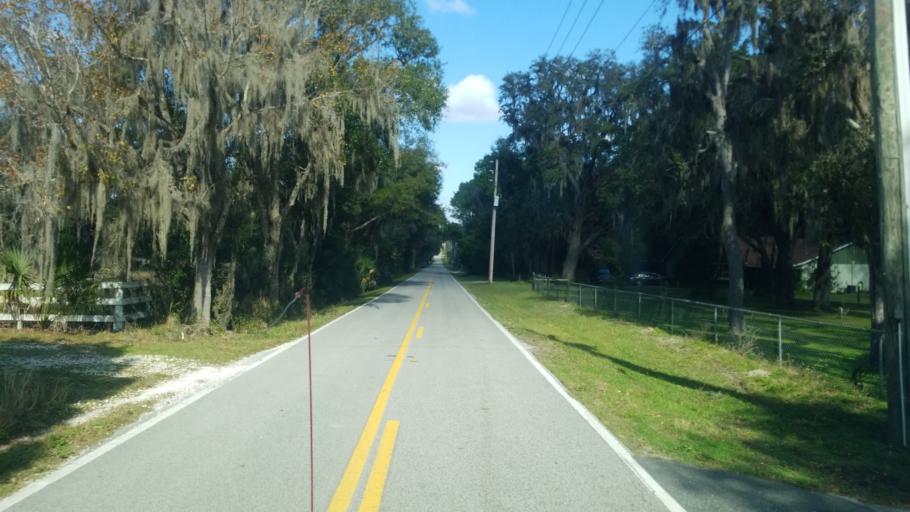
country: US
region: Florida
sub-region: Hernando County
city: North Brooksville
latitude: 28.6087
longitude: -82.3801
